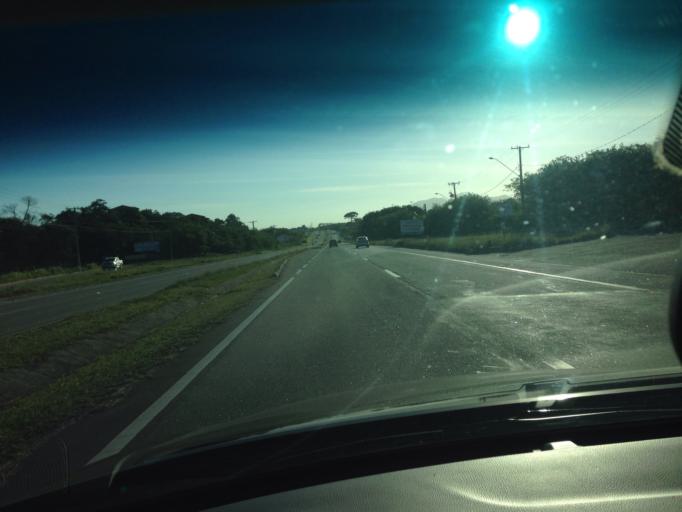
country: BR
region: Espirito Santo
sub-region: Viana
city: Viana
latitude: -20.5246
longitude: -40.3757
